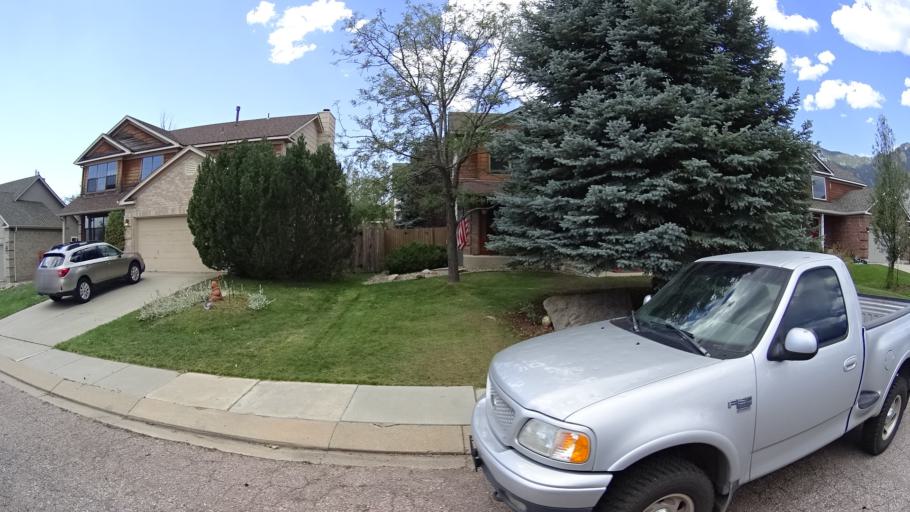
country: US
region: Colorado
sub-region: El Paso County
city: Fort Carson
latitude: 38.7630
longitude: -104.8177
